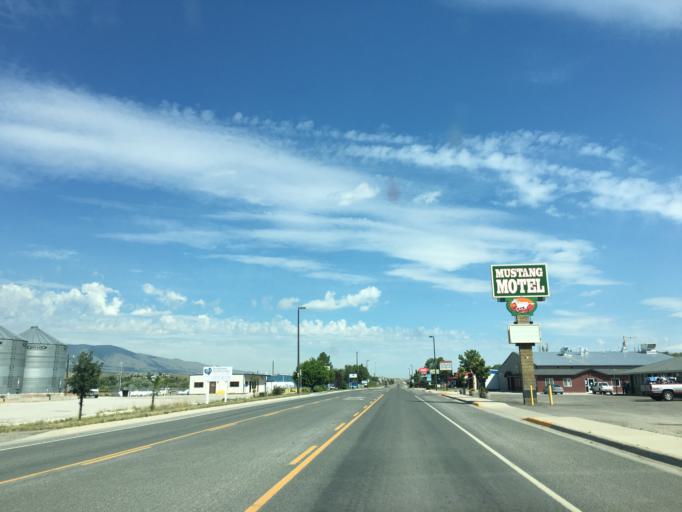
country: US
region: Montana
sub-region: Broadwater County
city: Townsend
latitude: 46.3231
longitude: -111.5241
